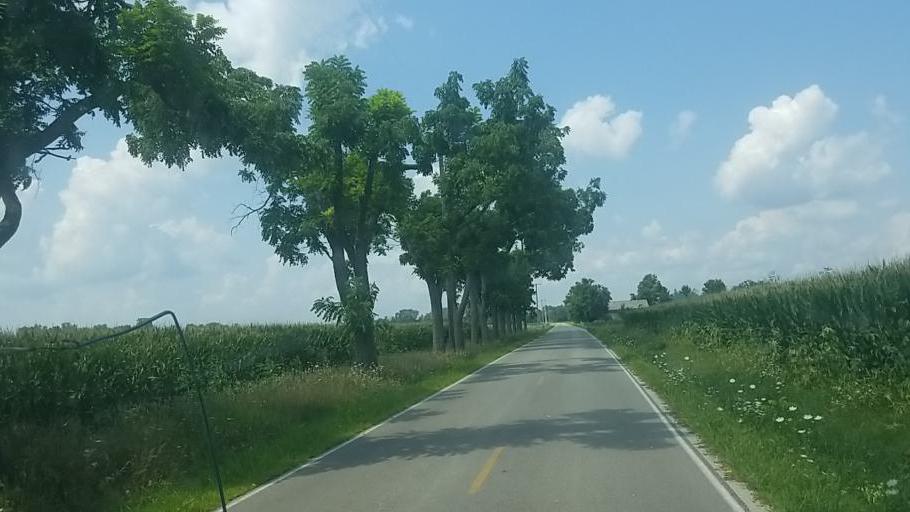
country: US
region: Ohio
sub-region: Crawford County
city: Crestline
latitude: 40.8087
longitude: -82.7344
